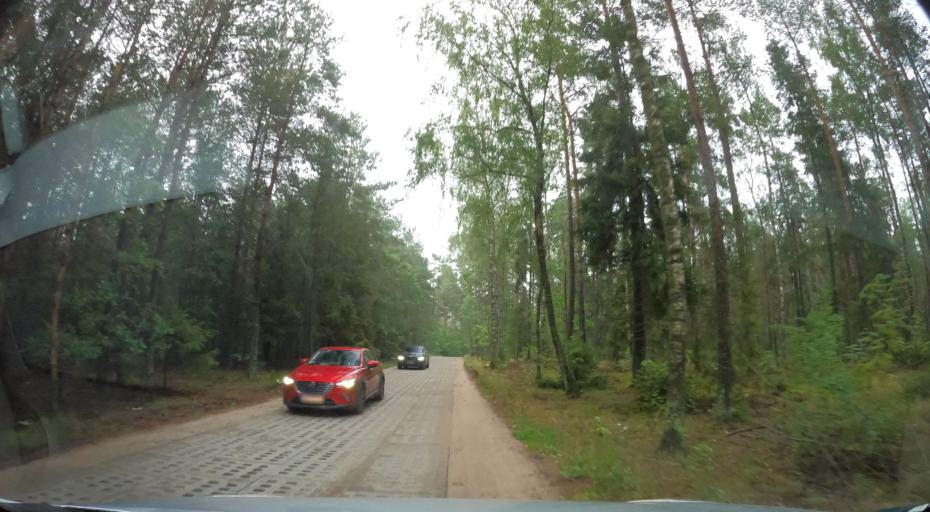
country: PL
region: Pomeranian Voivodeship
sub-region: Powiat kartuski
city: Chwaszczyno
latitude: 54.4198
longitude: 18.4241
